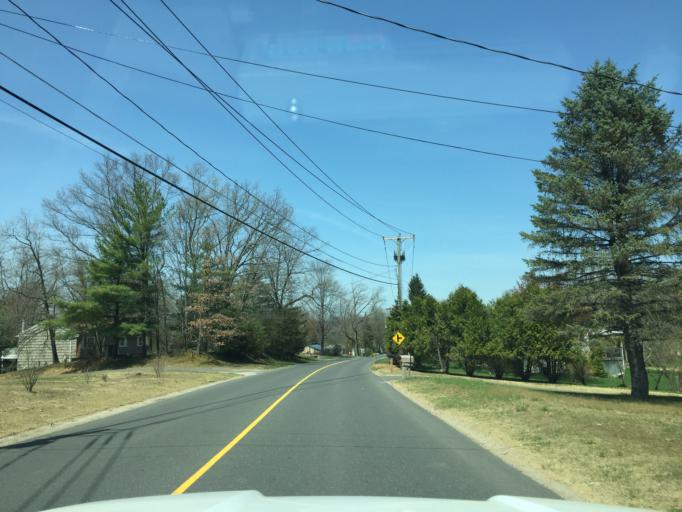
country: US
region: Connecticut
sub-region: Fairfield County
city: Bethel
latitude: 41.3965
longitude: -73.4035
